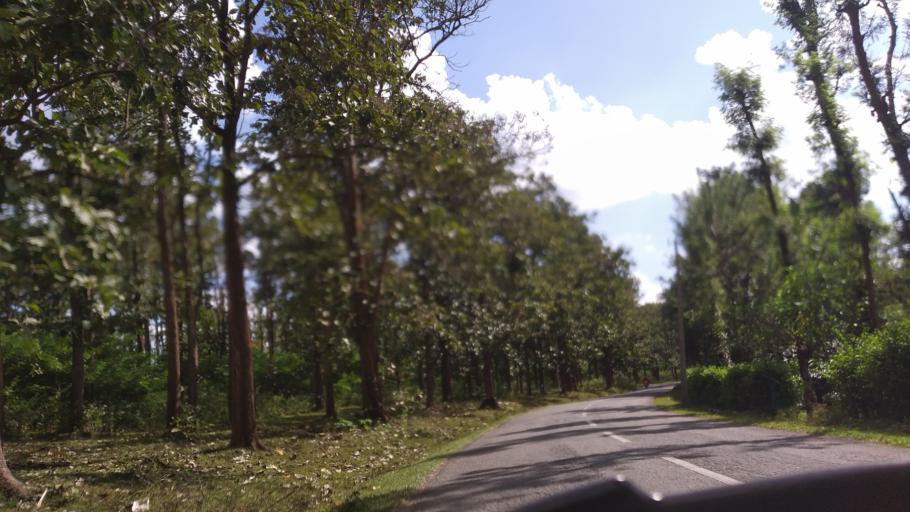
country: IN
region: Kerala
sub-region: Wayanad
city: Panamaram
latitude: 11.9376
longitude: 76.0648
